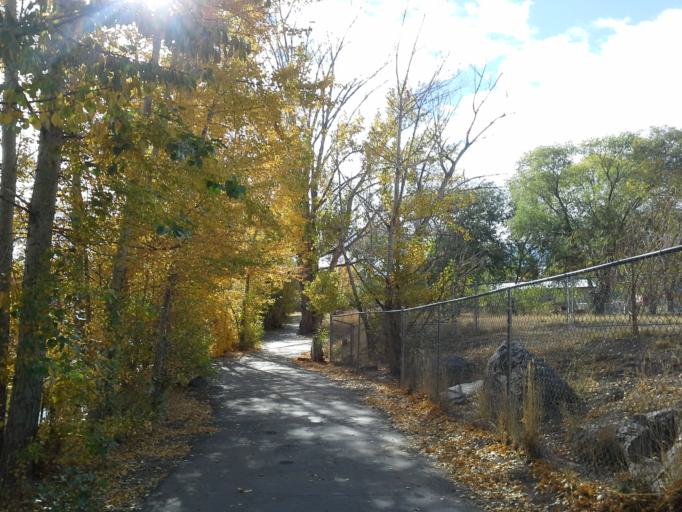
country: US
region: Oregon
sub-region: Baker County
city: Baker City
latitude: 44.7839
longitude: -117.8281
